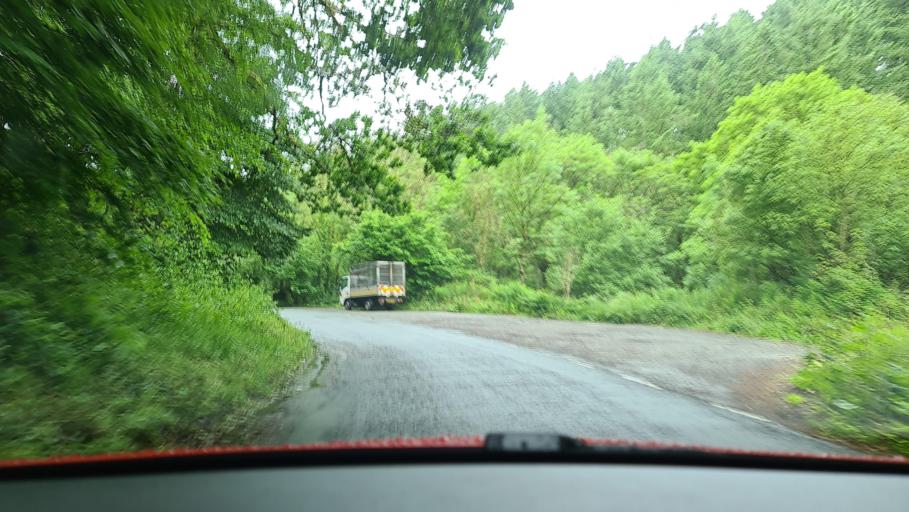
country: GB
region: England
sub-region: Cornwall
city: Liskeard
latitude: 50.4670
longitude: -4.5593
